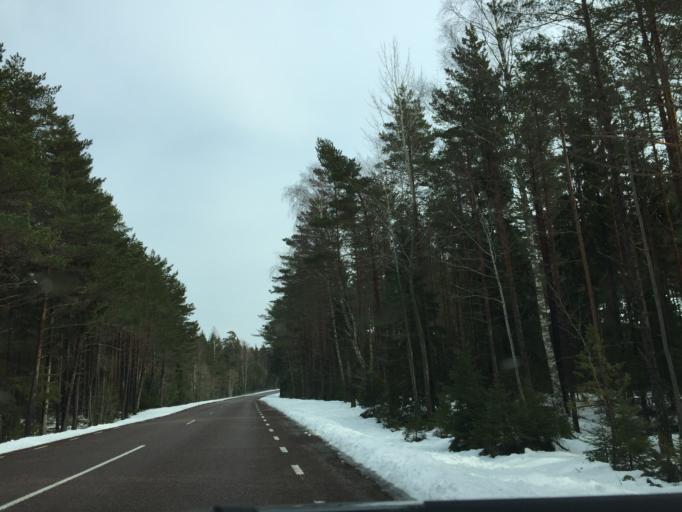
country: EE
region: Saare
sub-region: Kuressaare linn
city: Kuressaare
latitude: 58.3952
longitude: 22.1773
